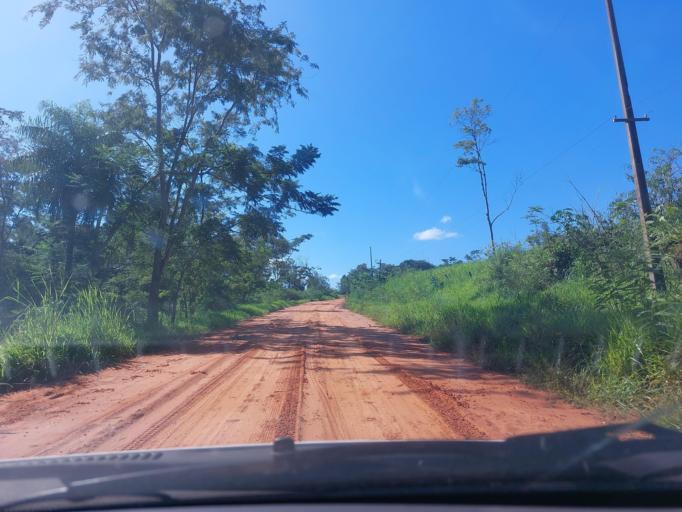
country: PY
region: San Pedro
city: Itacurubi del Rosario
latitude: -24.5430
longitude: -56.5840
